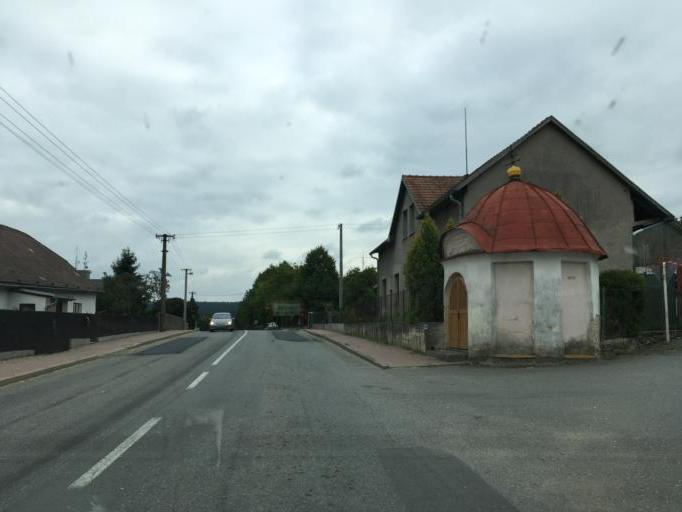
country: CZ
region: Central Bohemia
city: Cechtice
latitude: 49.5566
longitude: 15.1178
